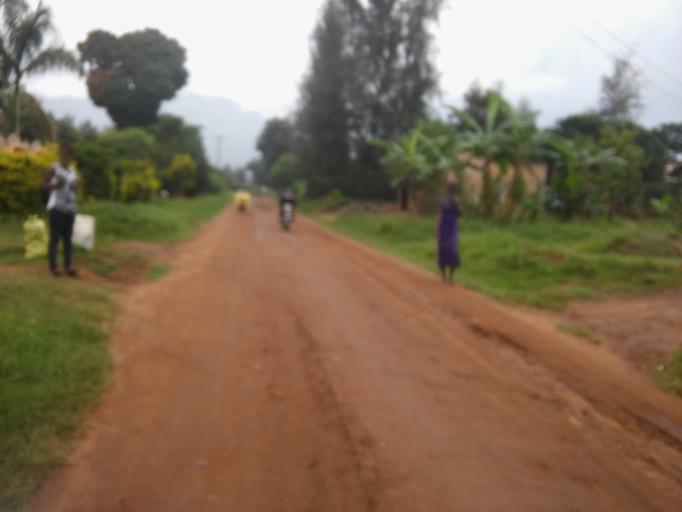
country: UG
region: Eastern Region
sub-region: Mbale District
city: Mbale
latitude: 1.0205
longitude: 34.1797
